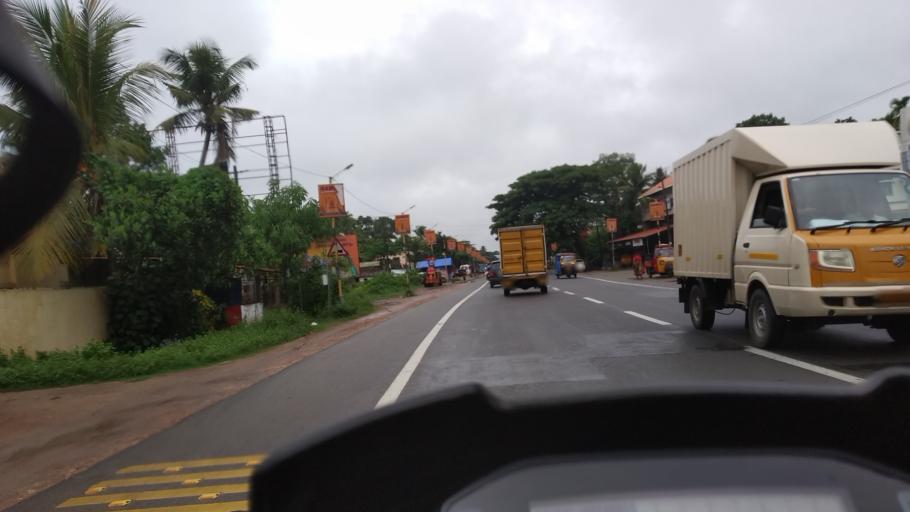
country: IN
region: Kerala
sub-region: Alappuzha
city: Mavelikara
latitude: 9.2814
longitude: 76.4525
